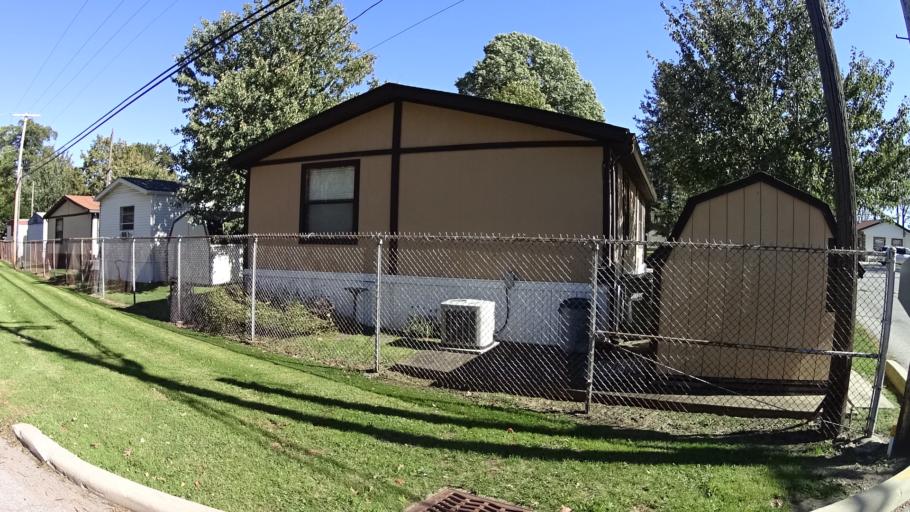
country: US
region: Ohio
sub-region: Lorain County
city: Amherst
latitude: 41.3944
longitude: -82.2506
